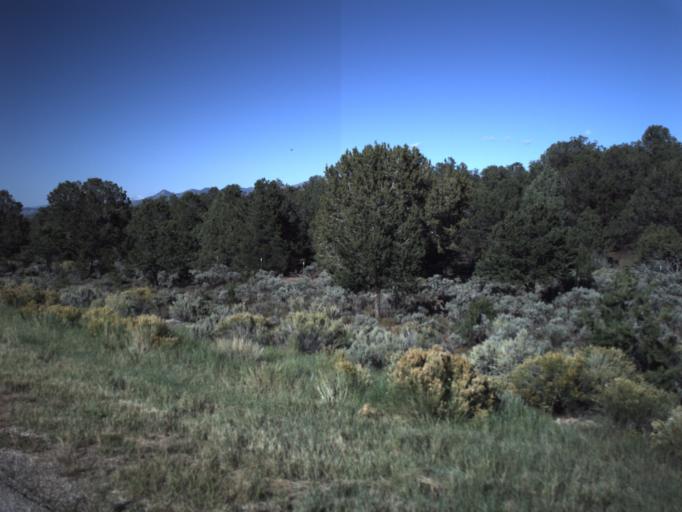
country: US
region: Utah
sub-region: Garfield County
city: Panguitch
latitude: 37.7876
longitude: -112.4395
